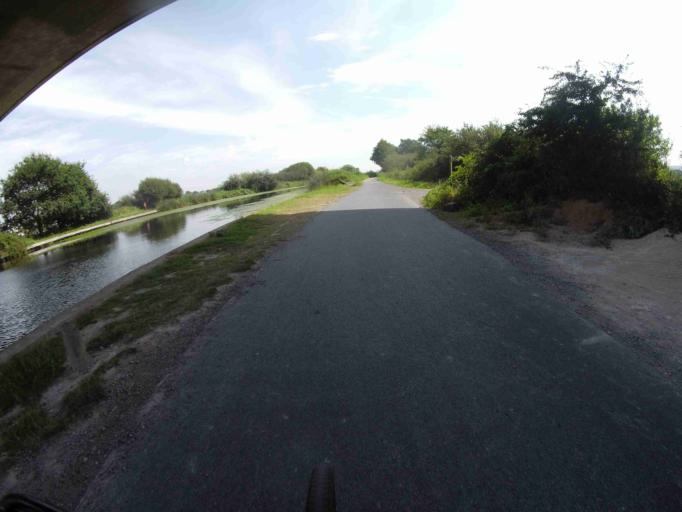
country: GB
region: England
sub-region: Devon
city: Topsham
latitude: 50.6880
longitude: -3.4826
